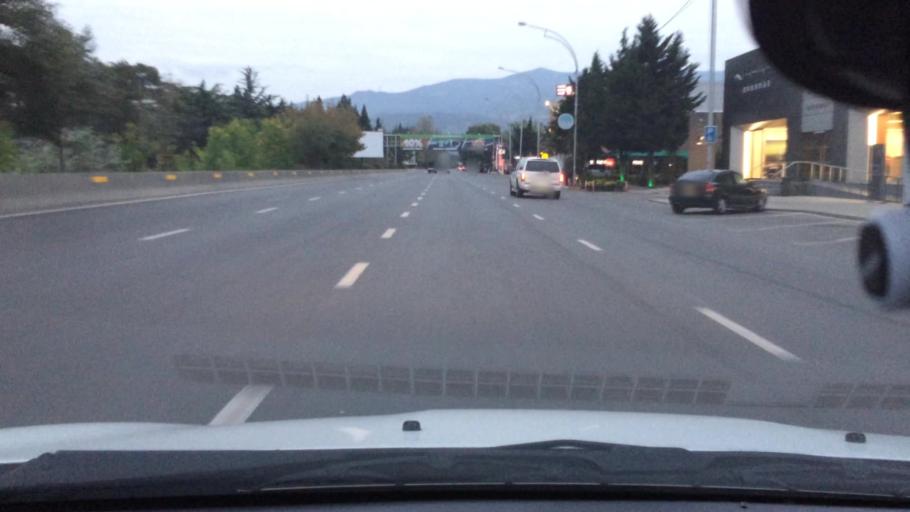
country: GE
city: Zahesi
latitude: 41.7960
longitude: 44.7708
